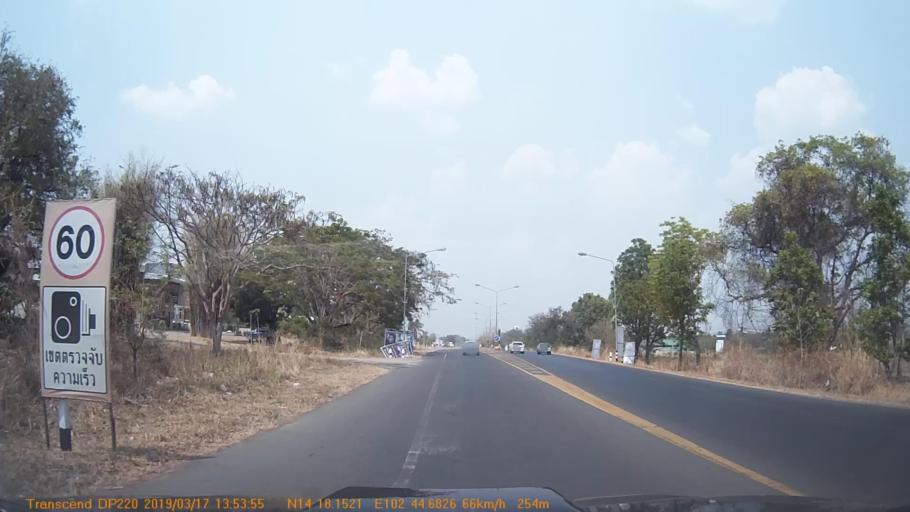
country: TH
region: Buriram
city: Non Din Daeng
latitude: 14.3028
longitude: 102.7448
